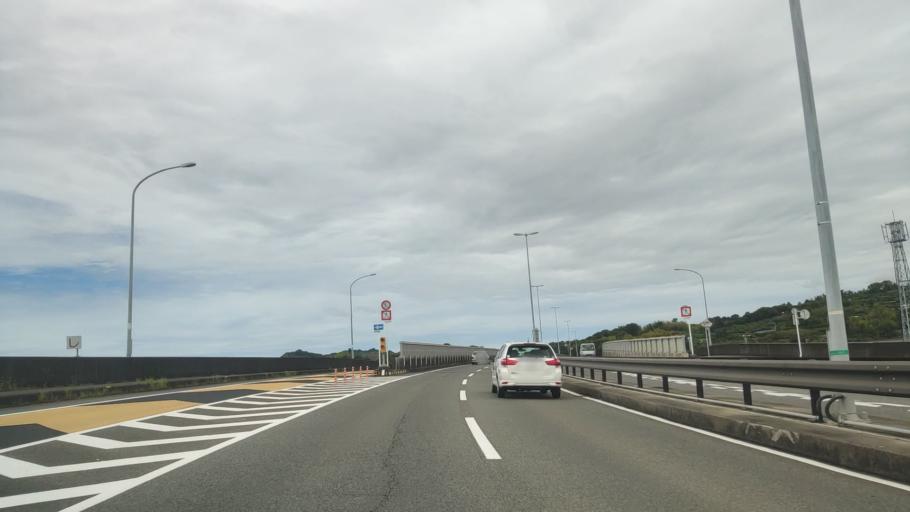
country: JP
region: Wakayama
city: Tanabe
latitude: 33.7415
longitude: 135.3879
